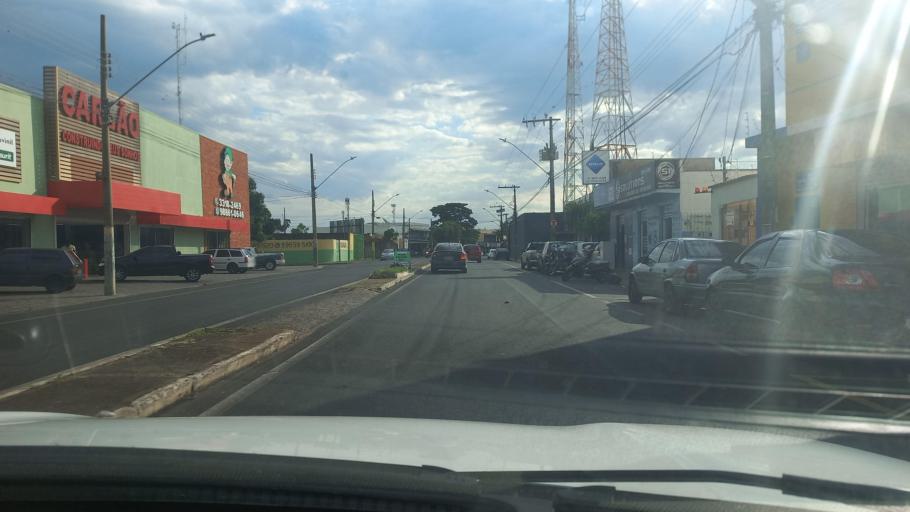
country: BR
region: Minas Gerais
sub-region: Uberaba
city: Uberaba
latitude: -19.7667
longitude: -47.9209
